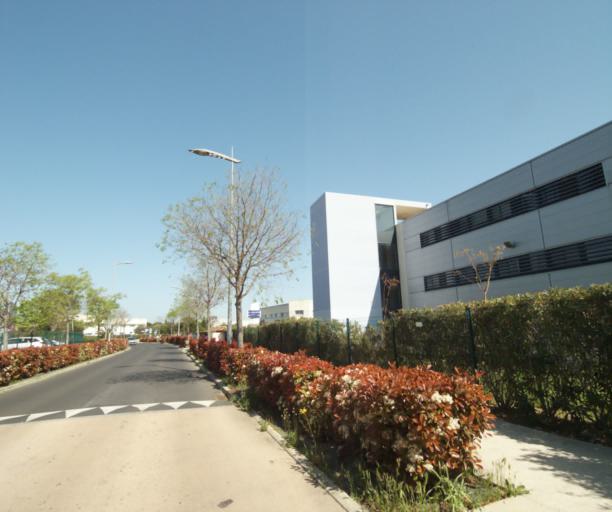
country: FR
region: Languedoc-Roussillon
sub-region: Departement de l'Herault
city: Perols
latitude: 43.5812
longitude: 3.9376
